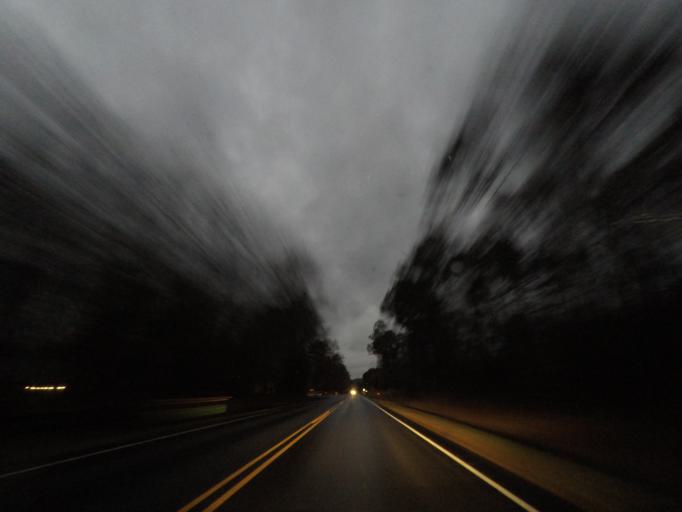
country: US
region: North Carolina
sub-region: Orange County
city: Hillsborough
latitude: 36.0455
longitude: -79.0218
